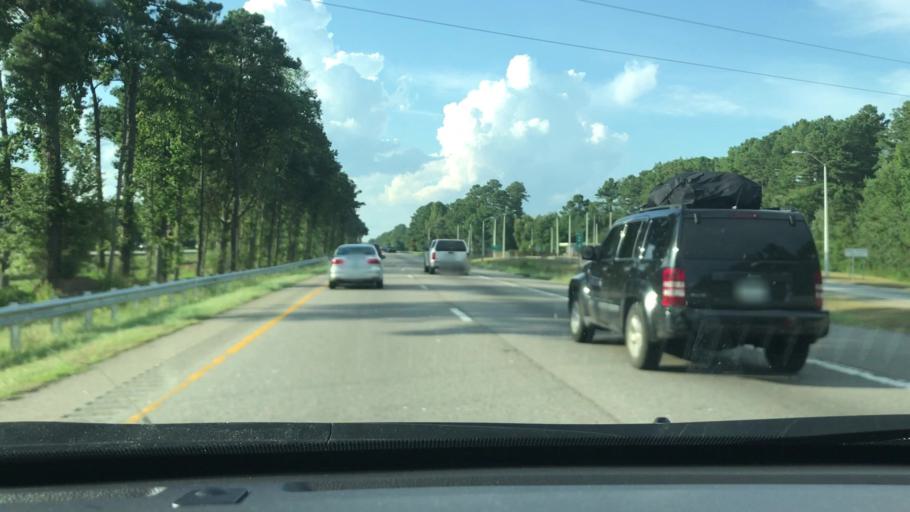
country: US
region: North Carolina
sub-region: Robeson County
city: Lumberton
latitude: 34.7048
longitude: -78.9978
